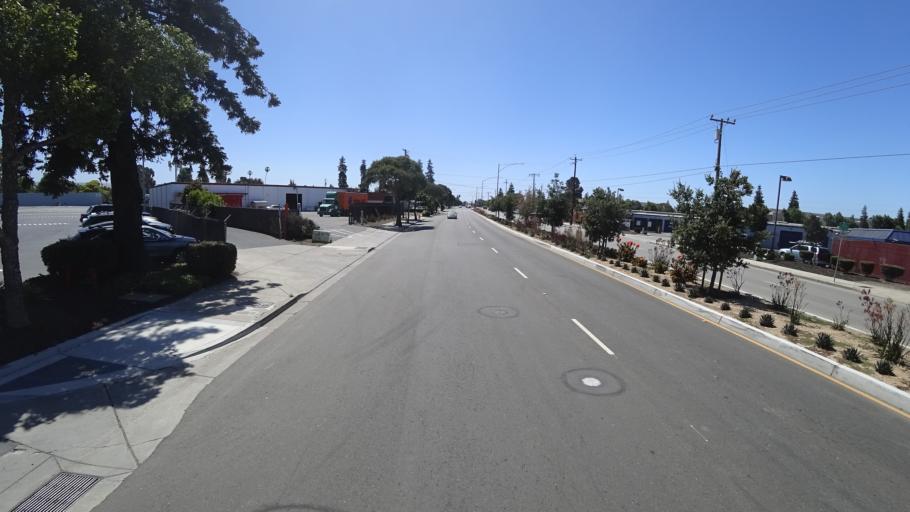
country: US
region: California
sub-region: Alameda County
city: San Lorenzo
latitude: 37.6398
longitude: -122.1184
